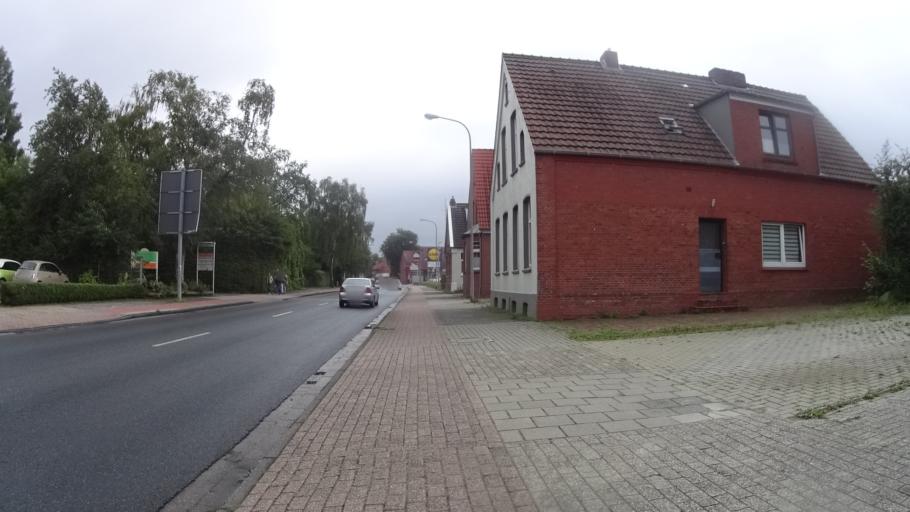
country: DE
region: Lower Saxony
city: Leer
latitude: 53.2303
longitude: 7.4381
